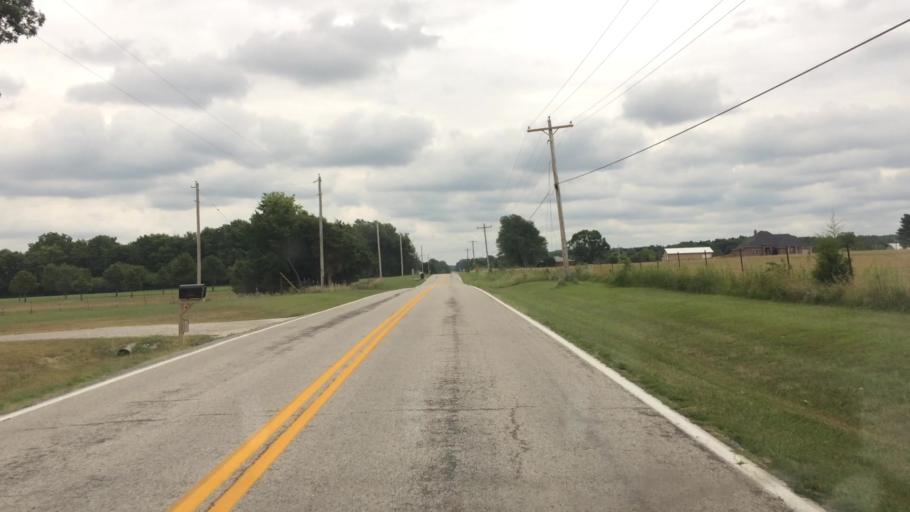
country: US
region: Missouri
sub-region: Greene County
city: Strafford
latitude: 37.2943
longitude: -93.2164
